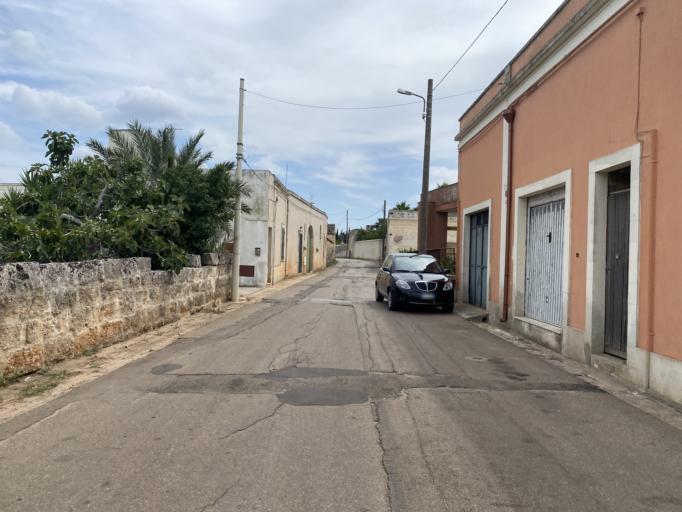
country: IT
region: Apulia
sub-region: Provincia di Lecce
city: Giuggianello
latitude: 40.0910
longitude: 18.3699
